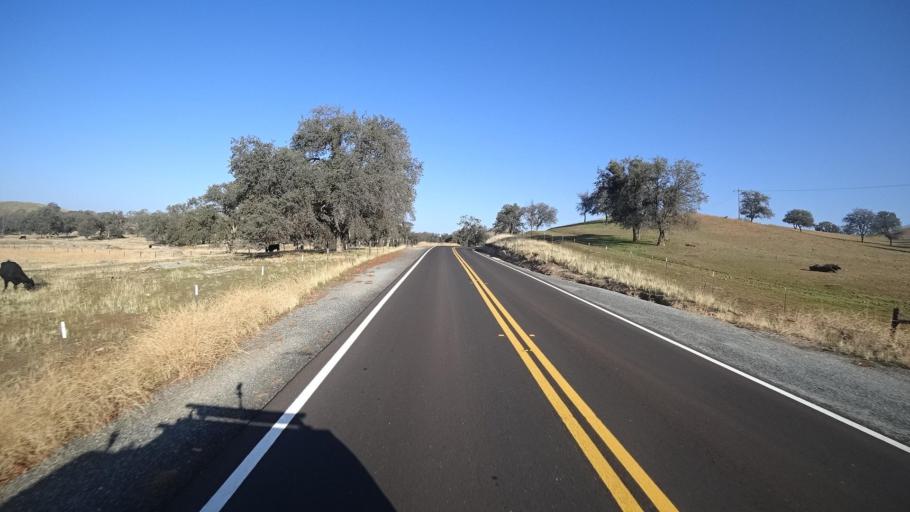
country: US
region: California
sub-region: Tulare County
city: Richgrove
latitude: 35.7325
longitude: -118.8598
